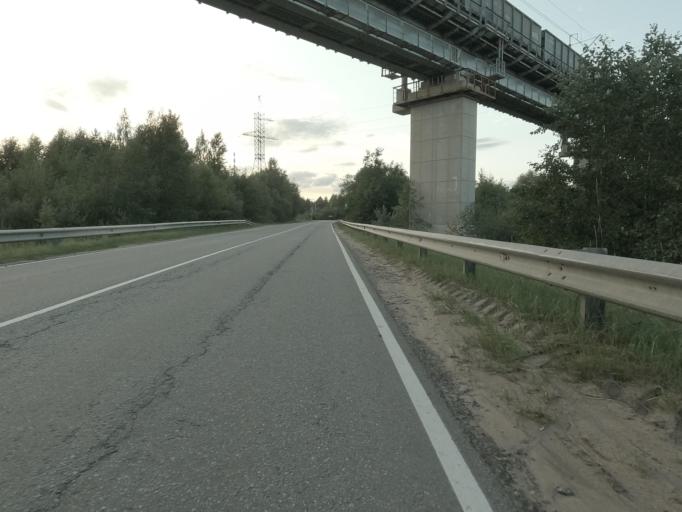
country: RU
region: Leningrad
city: Mga
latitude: 59.7584
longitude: 31.0183
